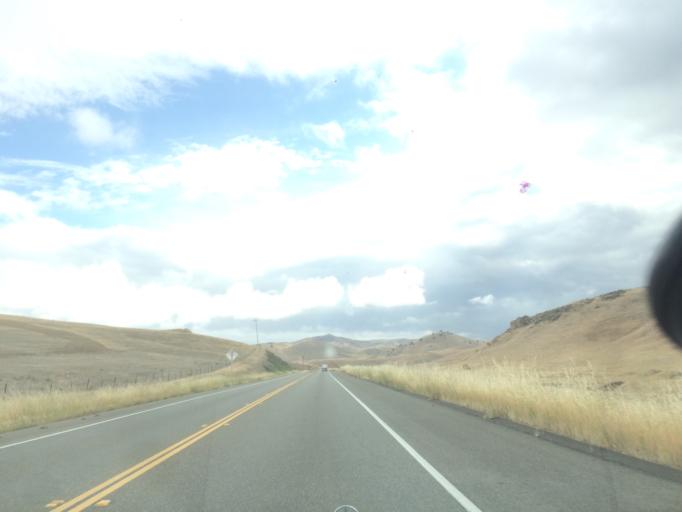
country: US
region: California
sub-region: San Luis Obispo County
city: Shandon
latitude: 35.7553
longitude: -120.2624
